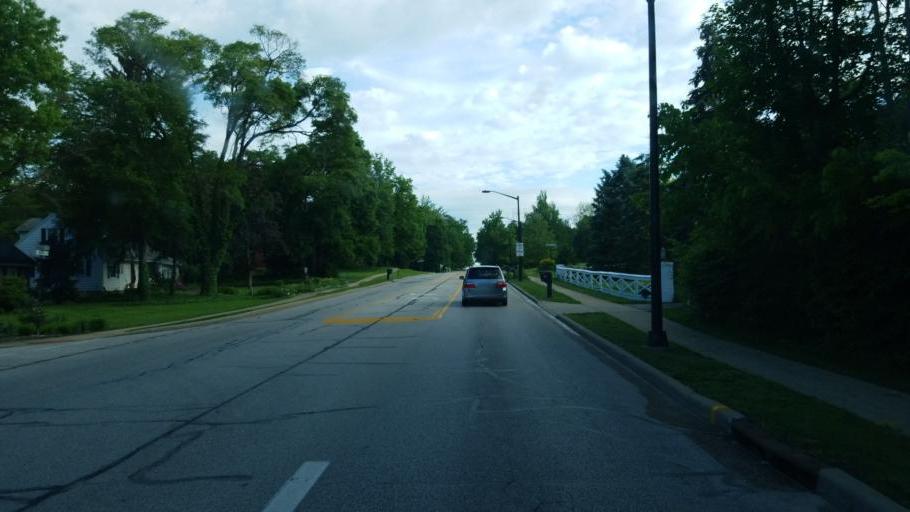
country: US
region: Ohio
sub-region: Summit County
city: Hudson
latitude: 41.2355
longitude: -81.4405
